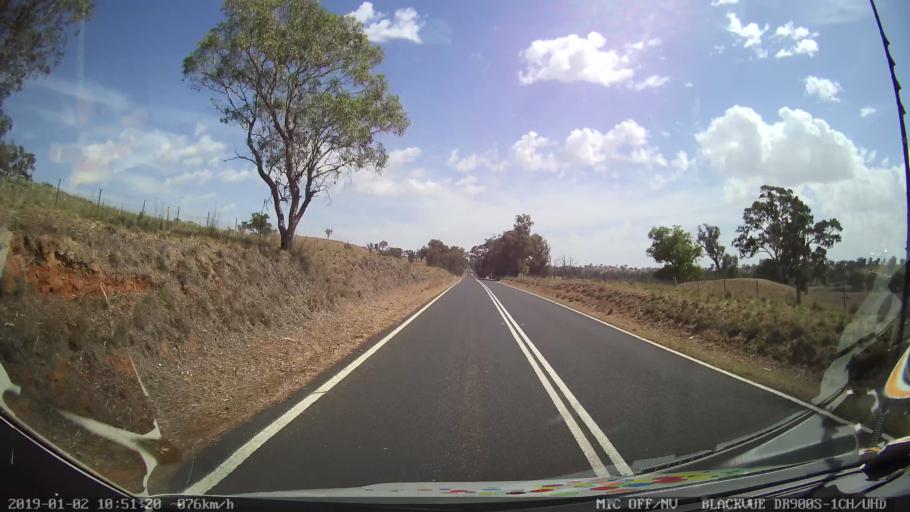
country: AU
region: New South Wales
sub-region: Cootamundra
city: Cootamundra
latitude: -34.7012
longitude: 148.2758
